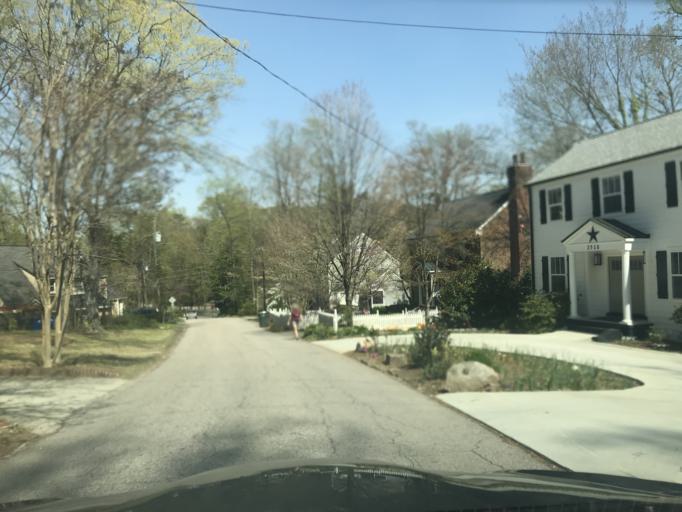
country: US
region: North Carolina
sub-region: Wake County
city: West Raleigh
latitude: 35.8117
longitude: -78.6411
